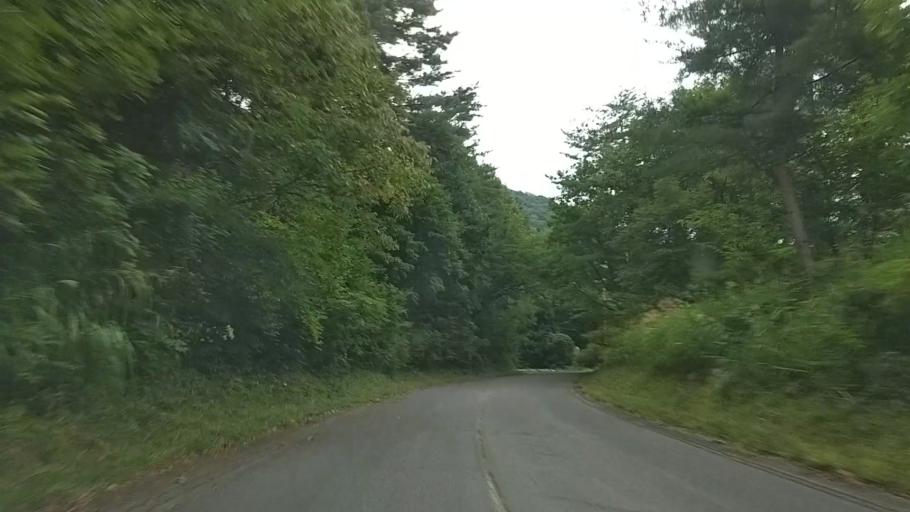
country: JP
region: Nagano
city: Iiyama
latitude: 36.8177
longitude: 138.3738
